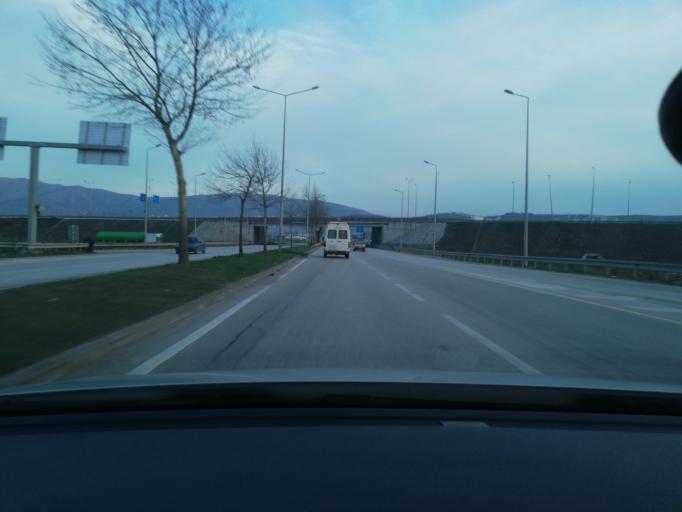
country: TR
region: Duzce
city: Konuralp
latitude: 40.8856
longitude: 31.1704
